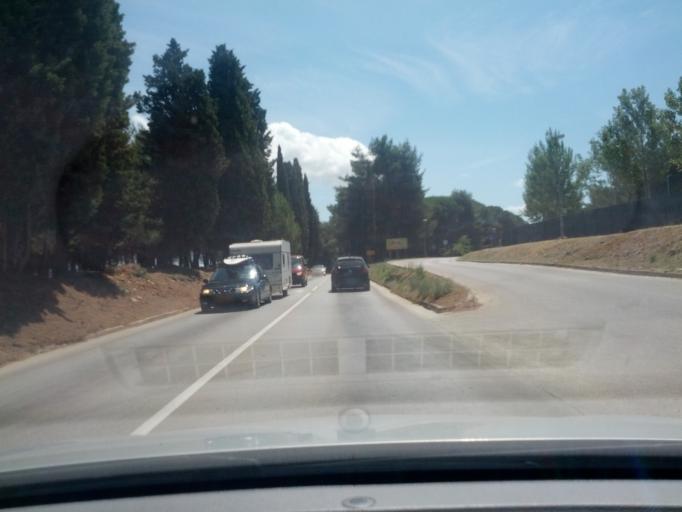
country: HR
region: Istarska
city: Fazana
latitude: 44.9191
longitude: 13.8098
